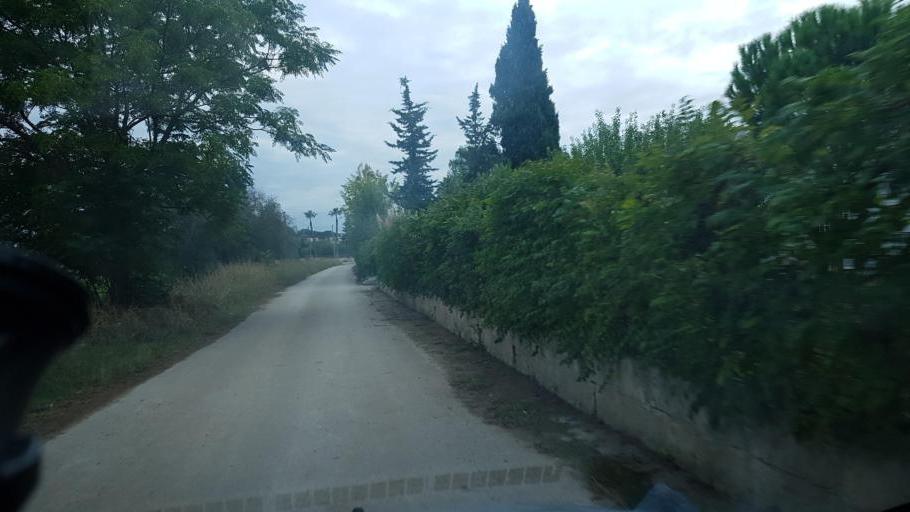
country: IT
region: Apulia
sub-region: Provincia di Brindisi
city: Oria
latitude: 40.5085
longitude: 17.6398
